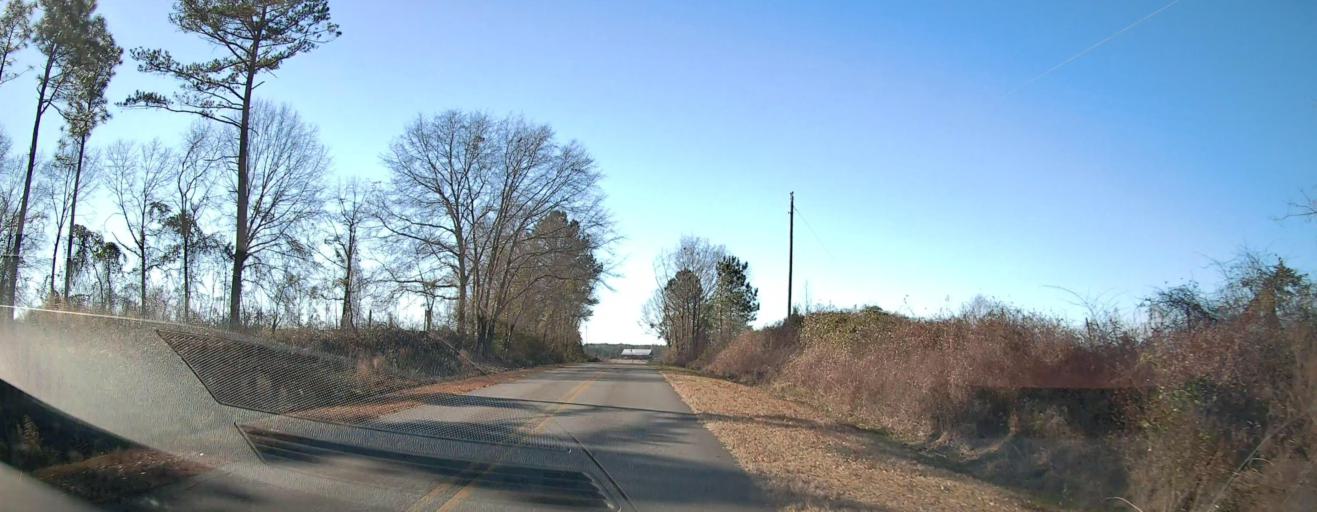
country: US
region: Georgia
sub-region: Taylor County
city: Butler
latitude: 32.6406
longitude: -84.3023
